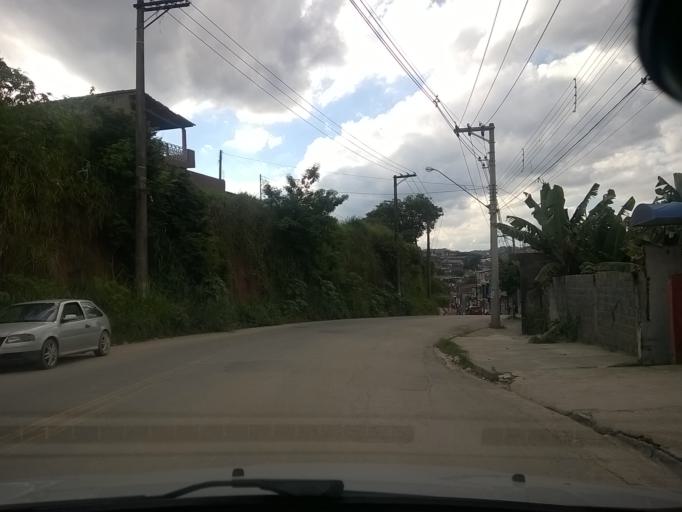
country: BR
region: Sao Paulo
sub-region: Francisco Morato
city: Francisco Morato
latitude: -23.2938
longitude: -46.7382
